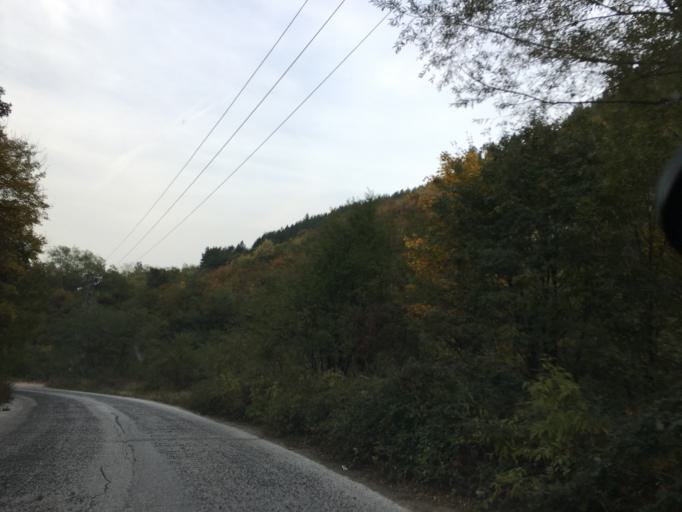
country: BG
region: Pazardzhik
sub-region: Obshtina Belovo
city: Belovo
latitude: 42.1762
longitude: 23.9828
